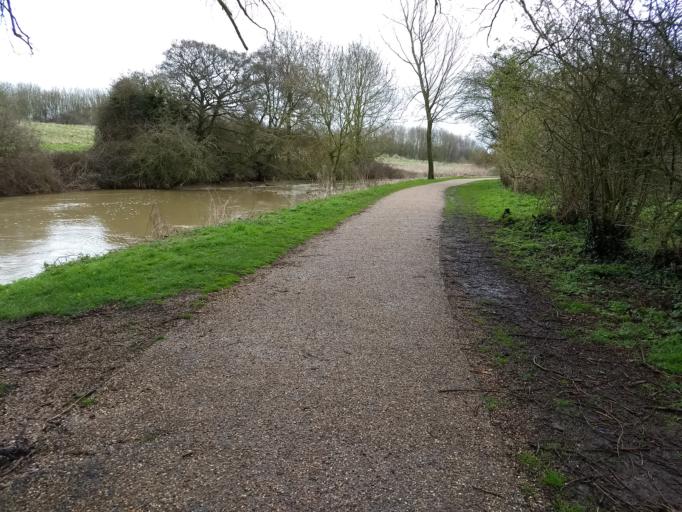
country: GB
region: England
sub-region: Milton Keynes
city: Stony Stratford
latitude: 52.0637
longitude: -0.8580
